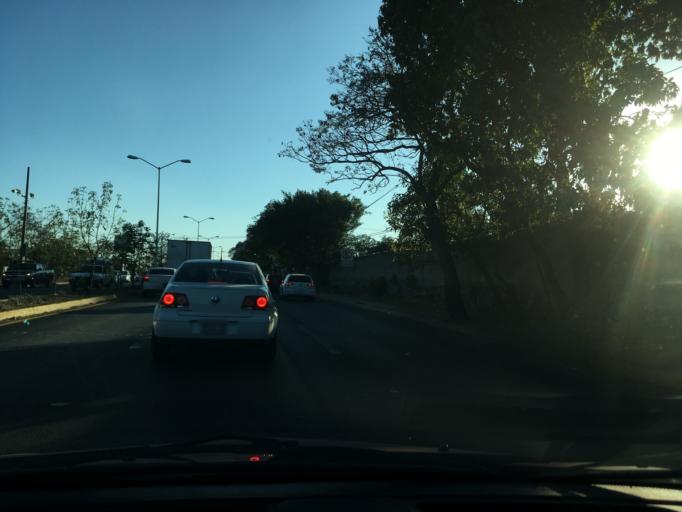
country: MX
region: Jalisco
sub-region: Tlajomulco de Zuniga
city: La Tijera
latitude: 20.5786
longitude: -103.4309
